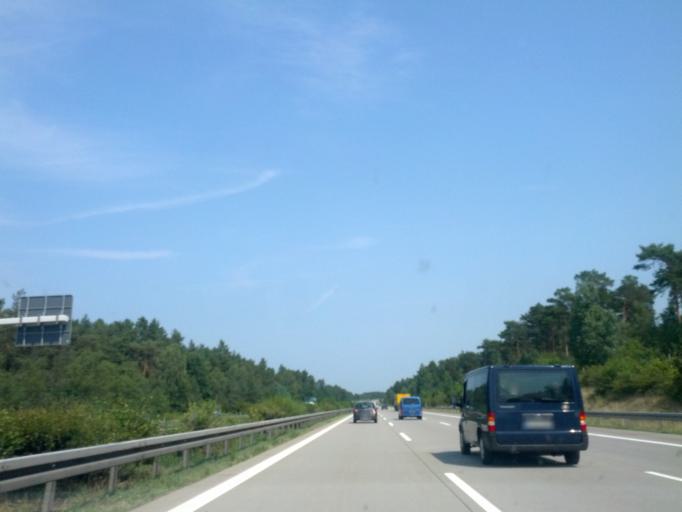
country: DE
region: Brandenburg
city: Niemegk
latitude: 52.1021
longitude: 12.7015
